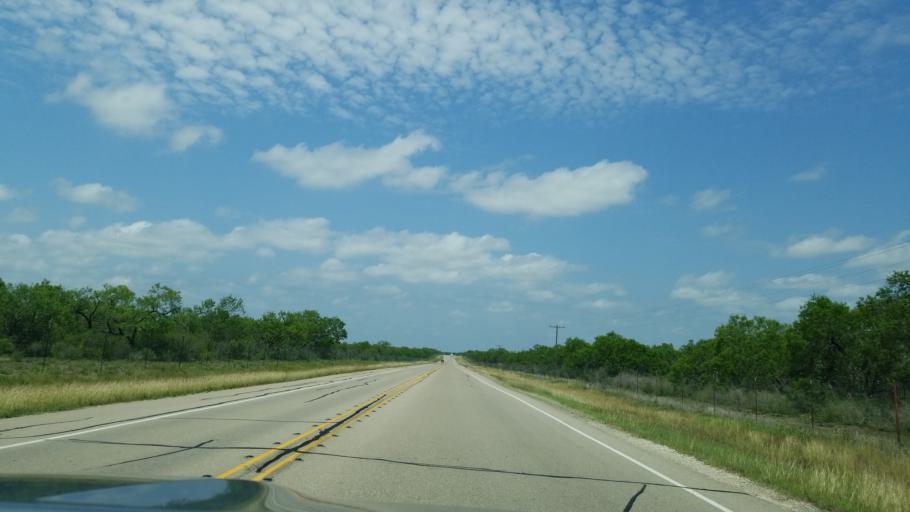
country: US
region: Texas
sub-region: Frio County
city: Pearsall
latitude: 29.0076
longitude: -99.1863
